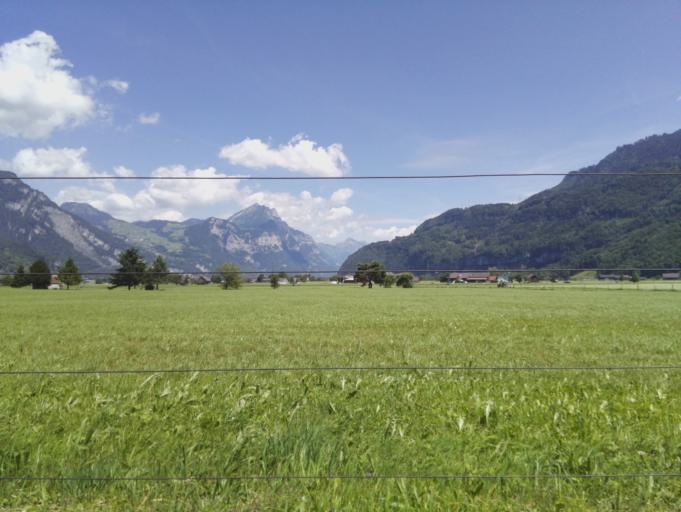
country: CH
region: Glarus
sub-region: Glarus
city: Oberurnen
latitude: 47.1224
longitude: 9.0656
